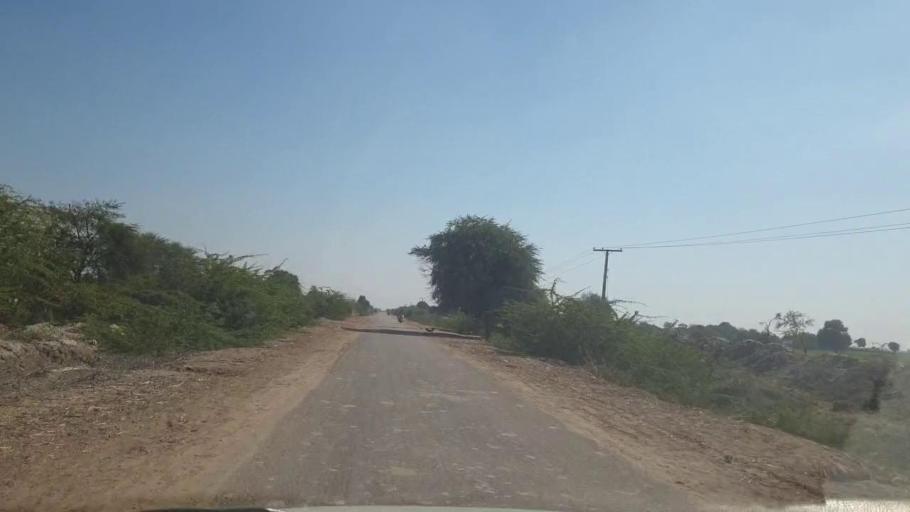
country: PK
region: Sindh
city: Mirpur Khas
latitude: 25.4754
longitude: 69.1744
